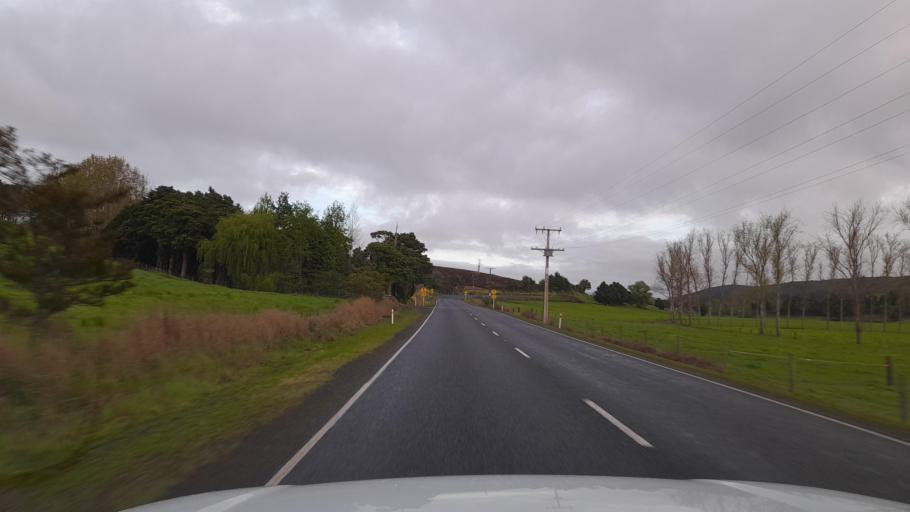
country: NZ
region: Northland
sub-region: Whangarei
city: Maungatapere
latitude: -35.7108
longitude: 174.0280
